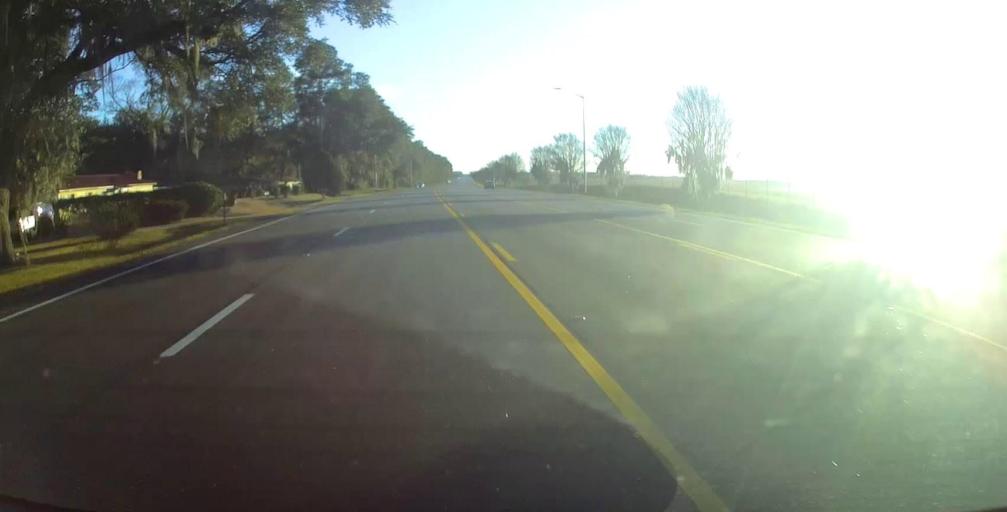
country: US
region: Georgia
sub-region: Dougherty County
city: Albany
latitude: 31.5429
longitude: -84.1792
